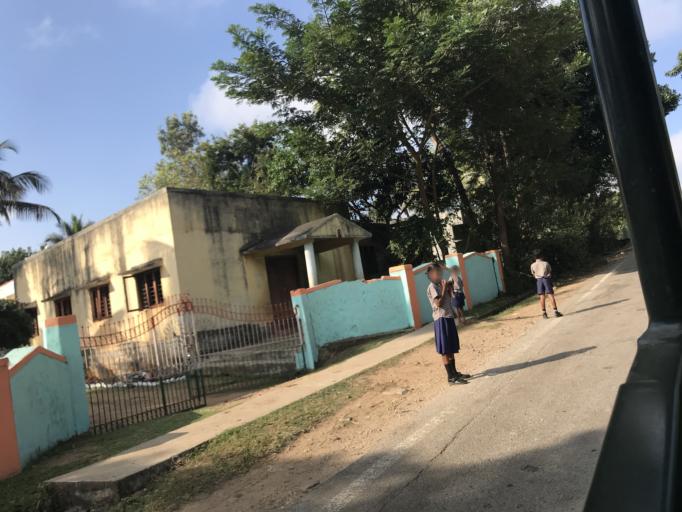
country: IN
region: Karnataka
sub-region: Mysore
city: Heggadadevankote
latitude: 11.9453
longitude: 76.2413
